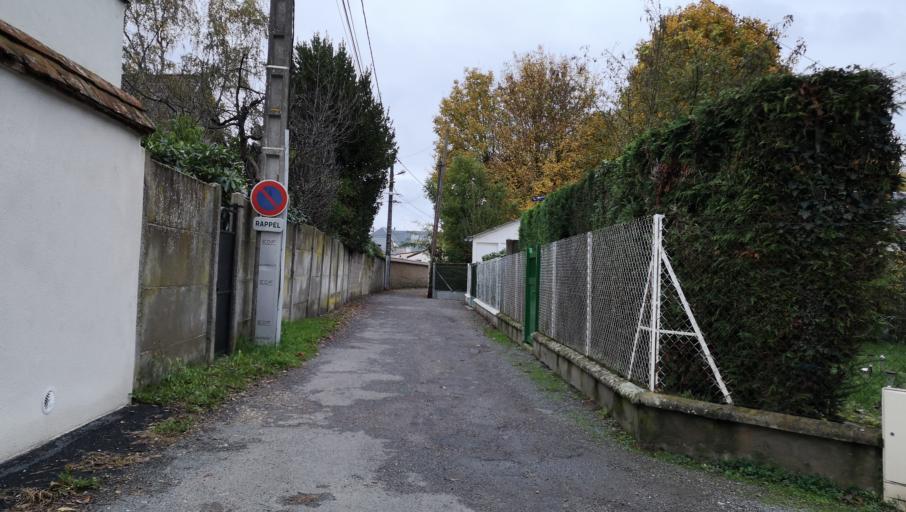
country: FR
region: Centre
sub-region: Departement du Loiret
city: Saint-Jean-le-Blanc
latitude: 47.9026
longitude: 1.9366
